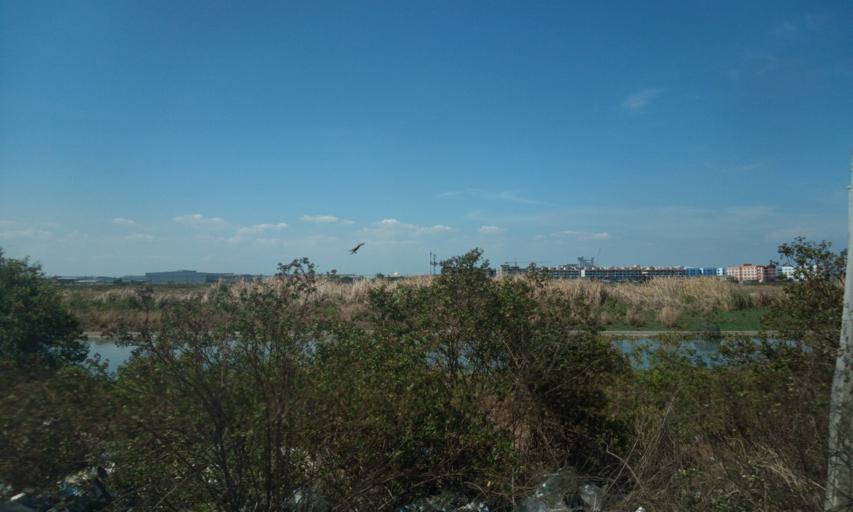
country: TH
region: Samut Prakan
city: Bang Bo District
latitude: 13.5545
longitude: 100.7770
